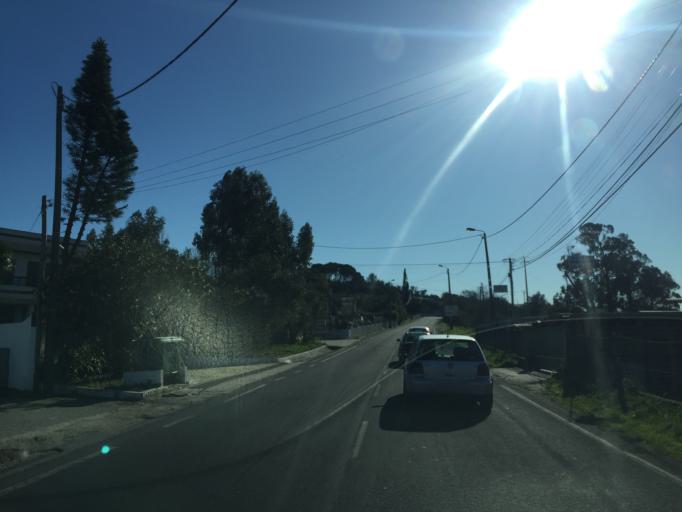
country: PT
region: Lisbon
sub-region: Sintra
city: Pero Pinheiro
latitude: 38.8381
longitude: -9.3114
